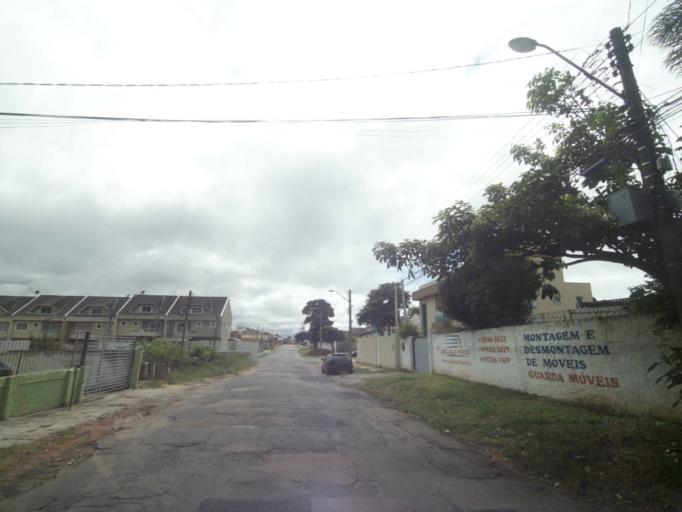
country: BR
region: Parana
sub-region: Curitiba
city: Curitiba
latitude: -25.4805
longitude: -49.2847
